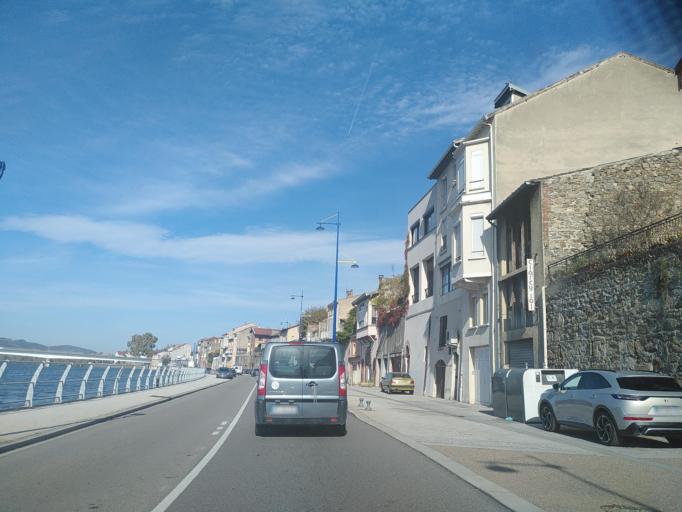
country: FR
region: Rhone-Alpes
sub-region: Departement de la Drome
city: Saint-Vallier
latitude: 45.1802
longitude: 4.8139
